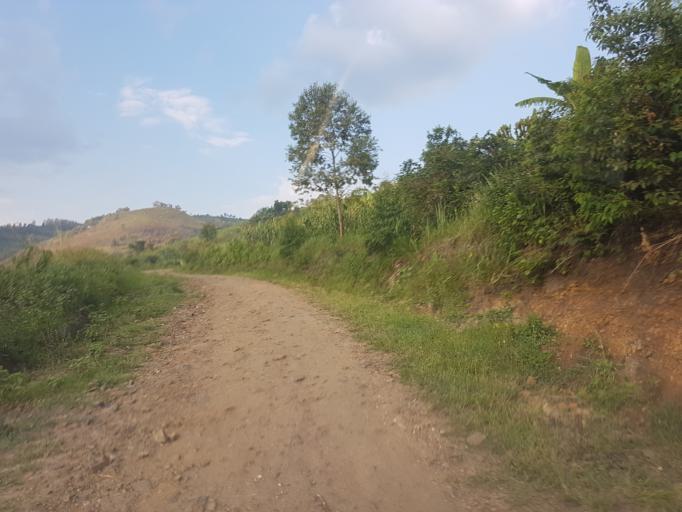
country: UG
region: Western Region
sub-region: Rukungiri District
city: Rukungiri
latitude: -0.6776
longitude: 29.9017
